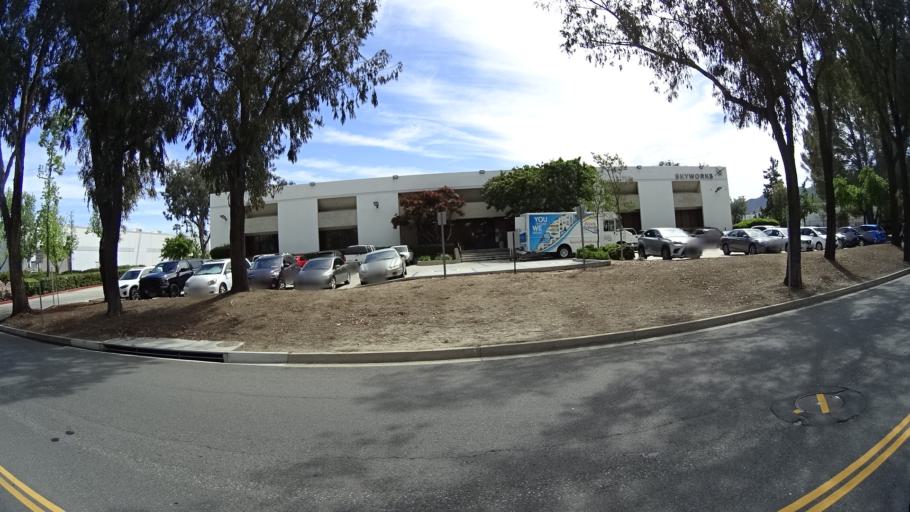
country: US
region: California
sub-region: Ventura County
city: Casa Conejo
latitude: 34.1884
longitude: -118.9300
